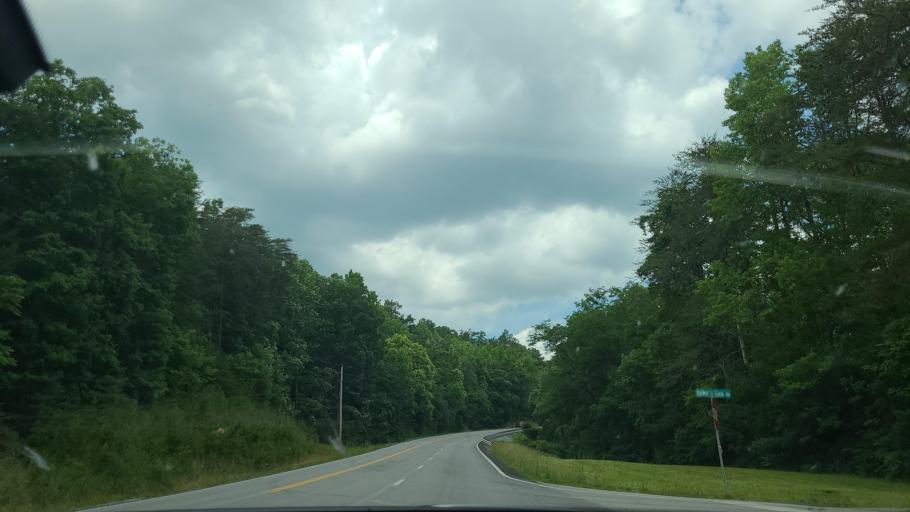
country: US
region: Tennessee
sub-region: Cumberland County
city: Lake Tansi
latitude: 35.7563
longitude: -85.0560
